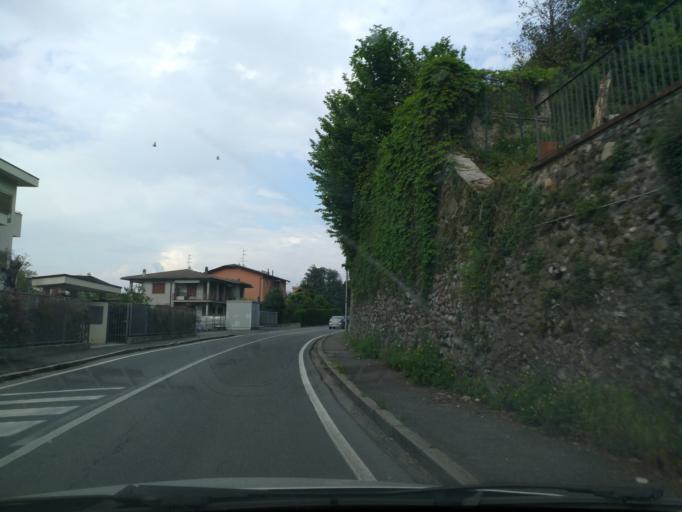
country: IT
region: Lombardy
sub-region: Provincia di Como
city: Figino Serenza
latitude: 45.7144
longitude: 9.1308
